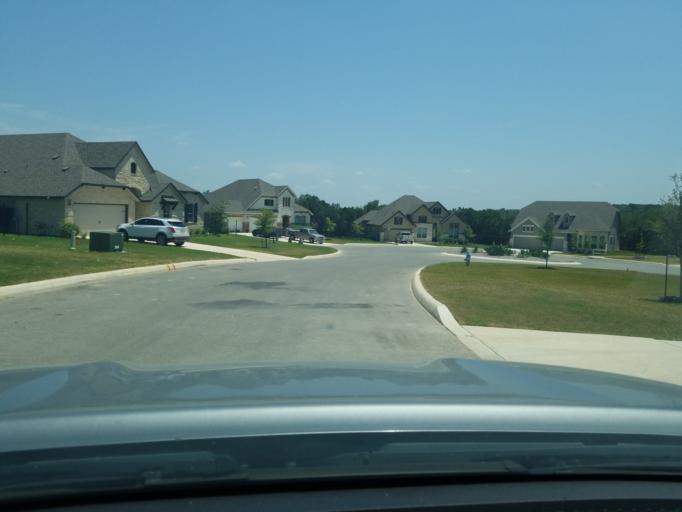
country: US
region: Texas
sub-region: Bexar County
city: Timberwood Park
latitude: 29.7167
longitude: -98.5117
